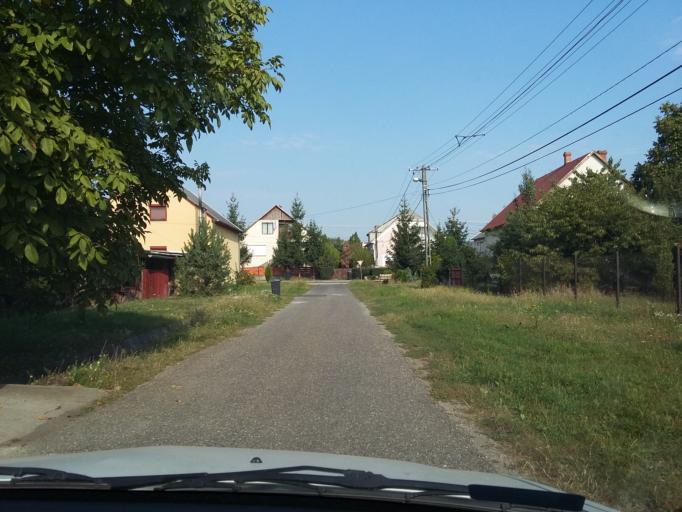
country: HU
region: Borsod-Abauj-Zemplen
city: Bekecs
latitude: 48.1509
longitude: 21.1803
